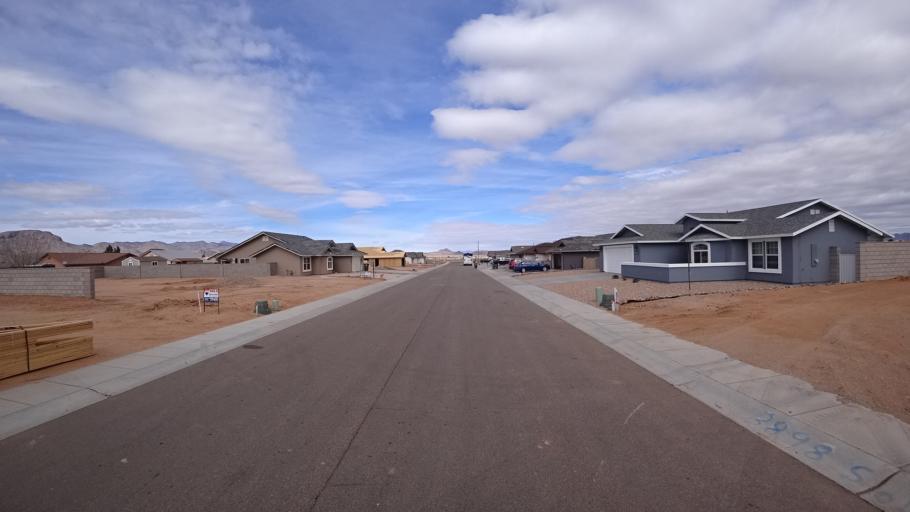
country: US
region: Arizona
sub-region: Mohave County
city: New Kingman-Butler
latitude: 35.2375
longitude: -113.9988
